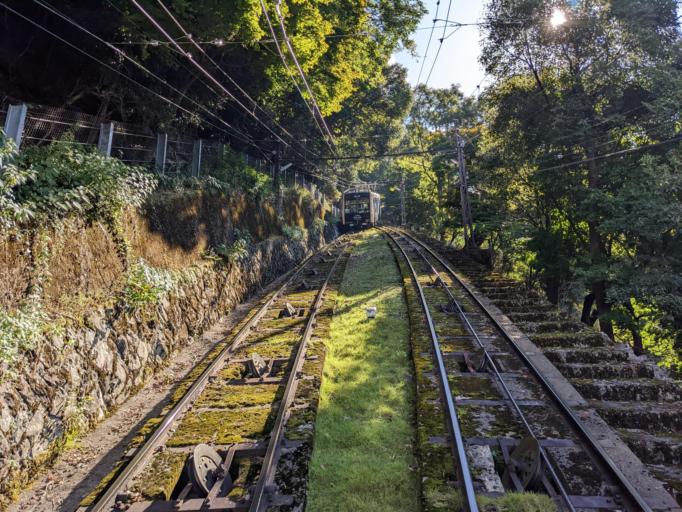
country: JP
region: Kyoto
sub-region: Kyoto-shi
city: Kamigyo-ku
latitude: 35.0662
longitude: 135.8155
